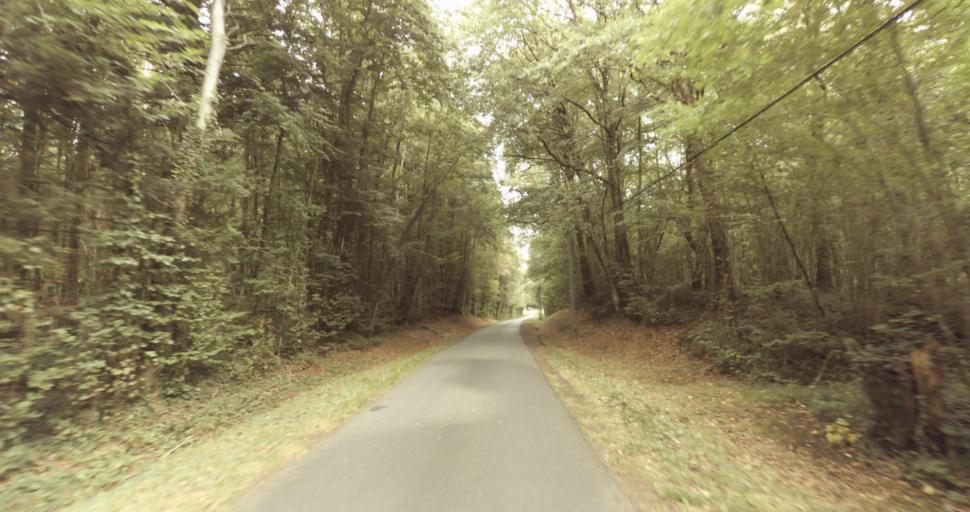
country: FR
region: Lower Normandy
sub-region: Departement de l'Orne
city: Gace
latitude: 48.6828
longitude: 0.2619
